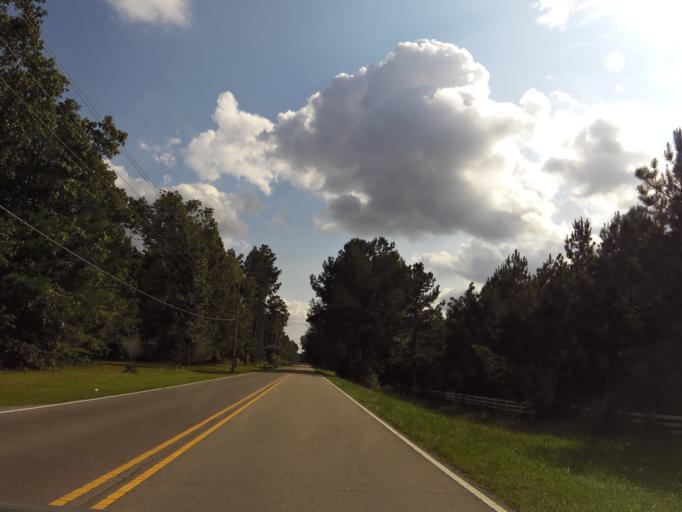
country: US
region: Mississippi
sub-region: Alcorn County
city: Corinth
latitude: 34.9613
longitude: -88.5165
